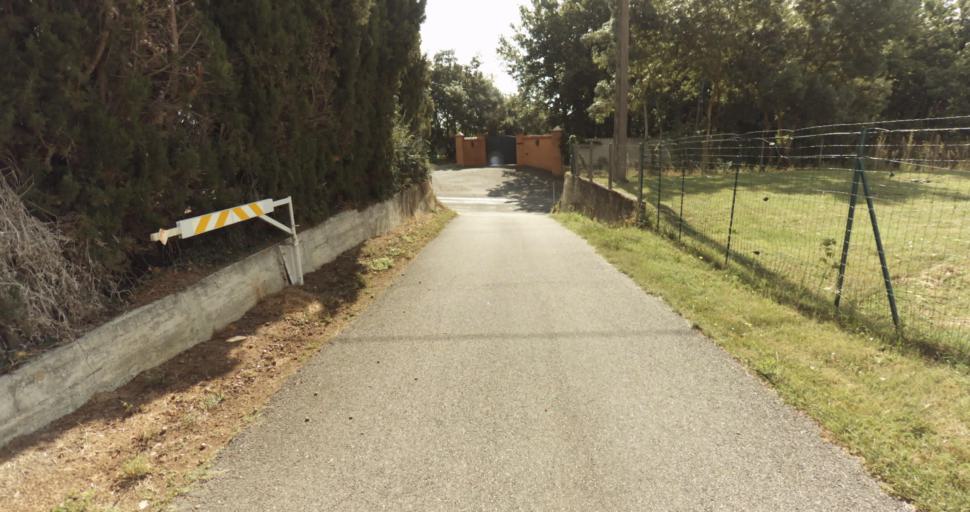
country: FR
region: Midi-Pyrenees
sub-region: Departement de la Haute-Garonne
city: Fonsorbes
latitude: 43.5670
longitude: 1.2332
